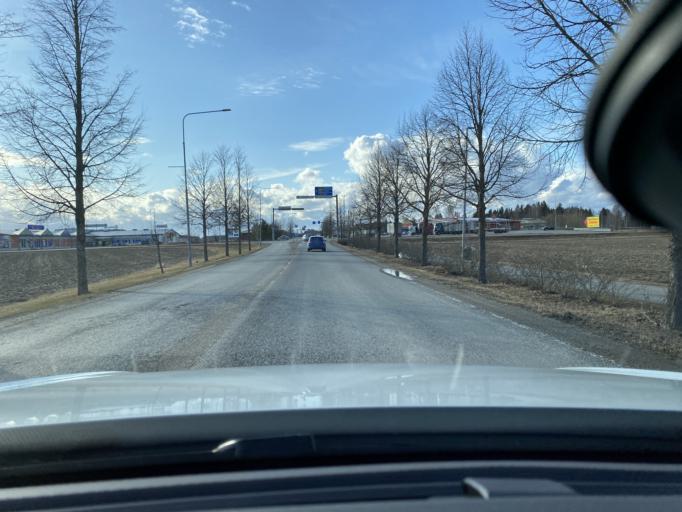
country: FI
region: Satakunta
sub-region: Pori
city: Huittinen
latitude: 61.1739
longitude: 22.6855
